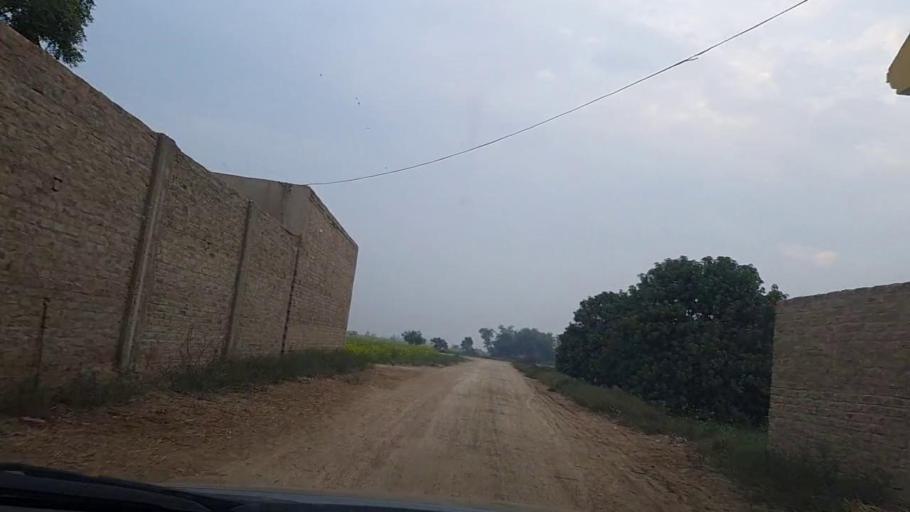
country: PK
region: Sindh
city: Sakrand
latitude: 26.2894
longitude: 68.2438
